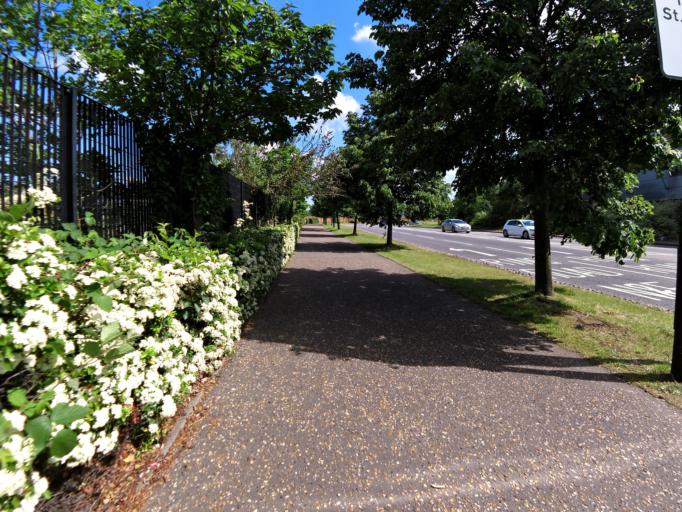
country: GB
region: England
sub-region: Norfolk
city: Thorpe Hamlet
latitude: 52.6248
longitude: 1.3089
